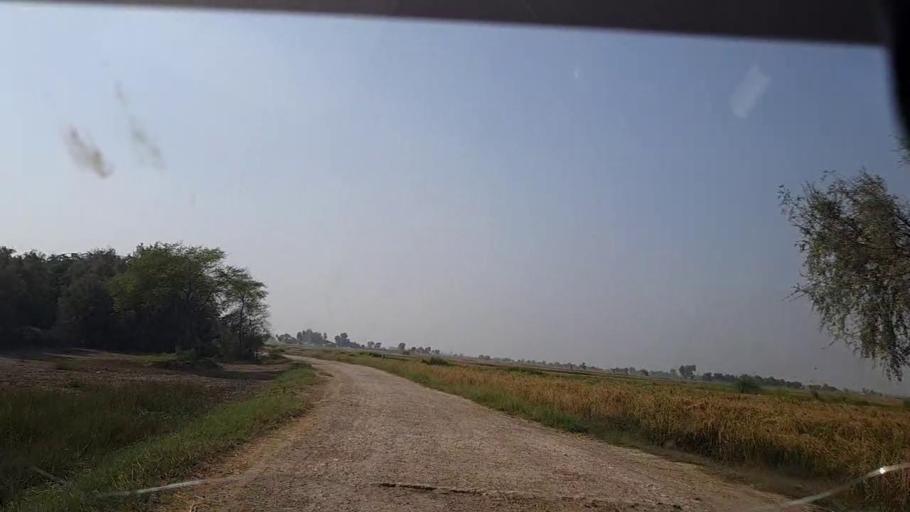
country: PK
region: Sindh
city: Shikarpur
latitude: 28.0914
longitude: 68.6034
